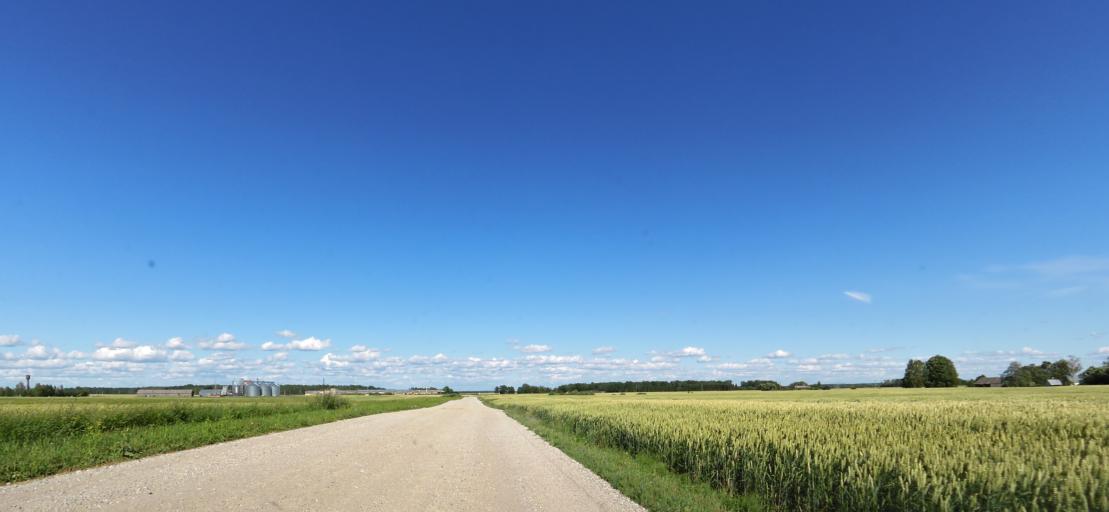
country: LT
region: Panevezys
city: Pasvalys
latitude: 56.1258
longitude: 24.3890
